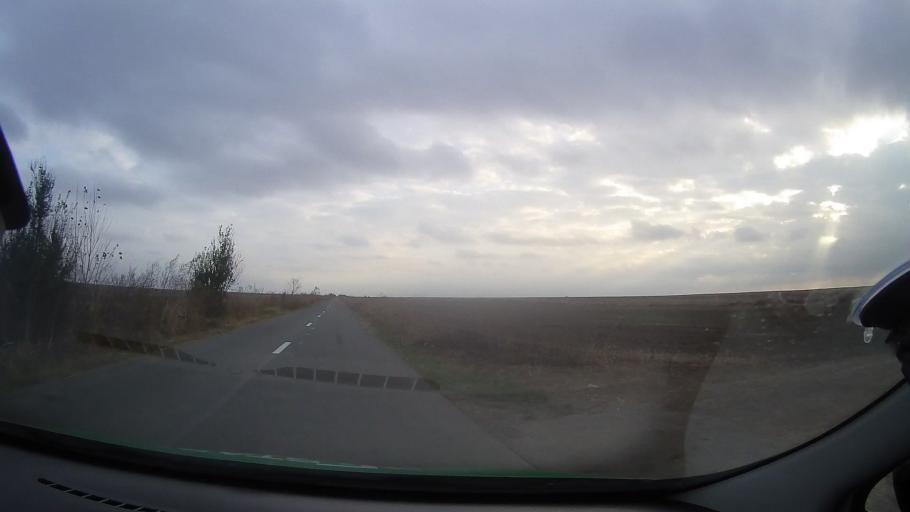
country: RO
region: Constanta
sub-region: Comuna Pestera
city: Pestera
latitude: 44.1467
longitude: 28.1151
